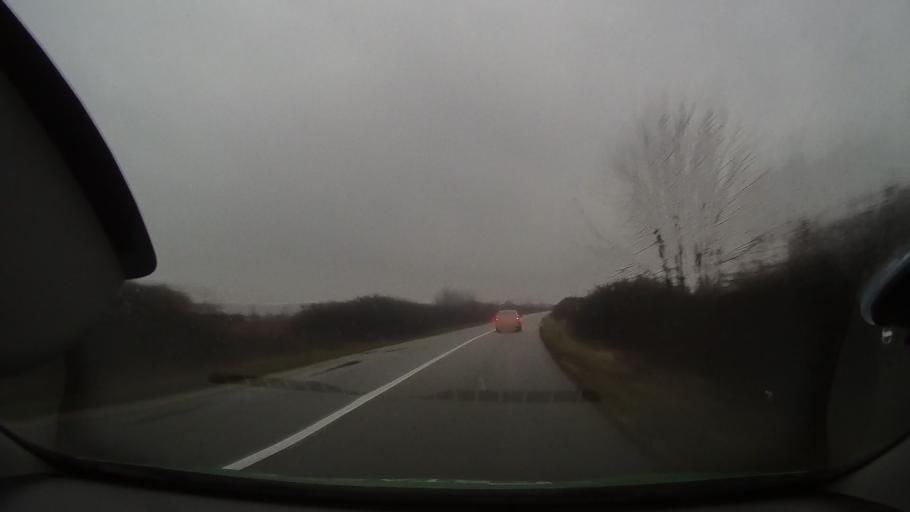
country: RO
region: Arad
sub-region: Comuna Craiova
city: Craiova
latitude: 46.5435
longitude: 21.9596
